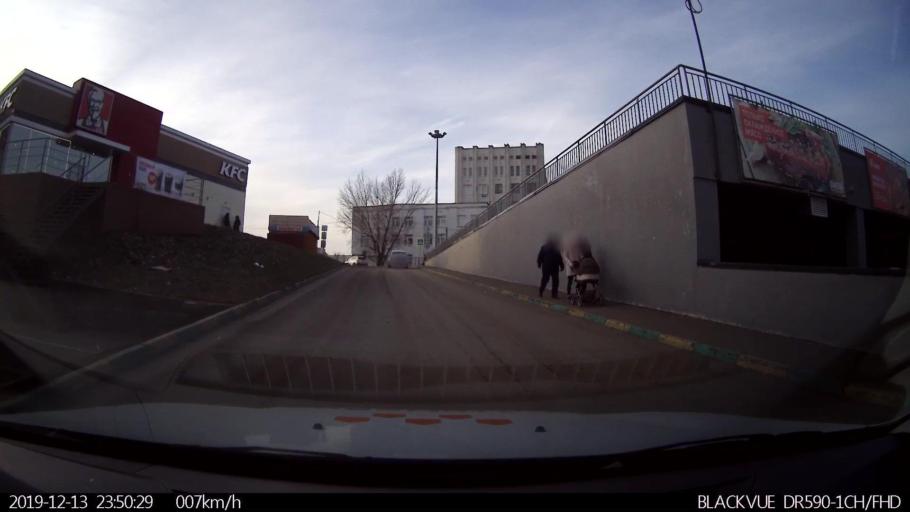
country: RU
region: Nizjnij Novgorod
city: Nizhniy Novgorod
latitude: 56.2997
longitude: 43.9471
